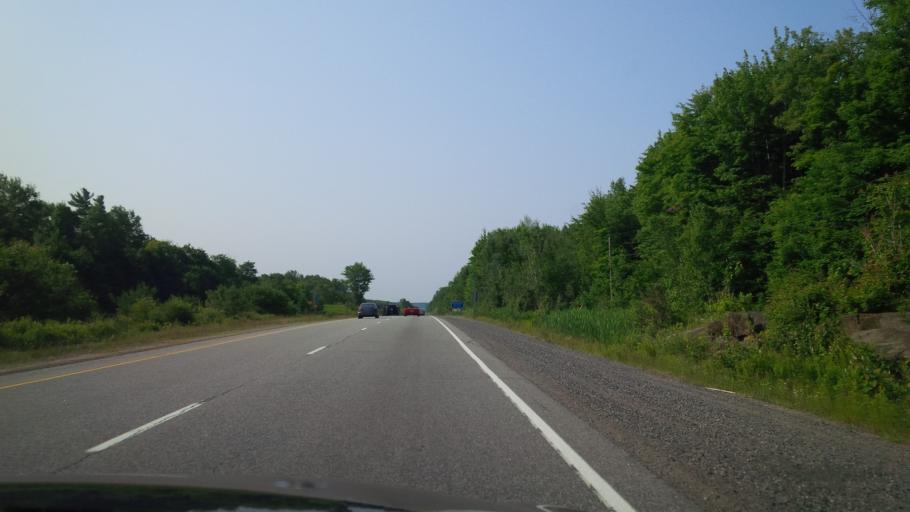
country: CA
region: Ontario
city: Bracebridge
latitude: 45.1541
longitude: -79.3118
